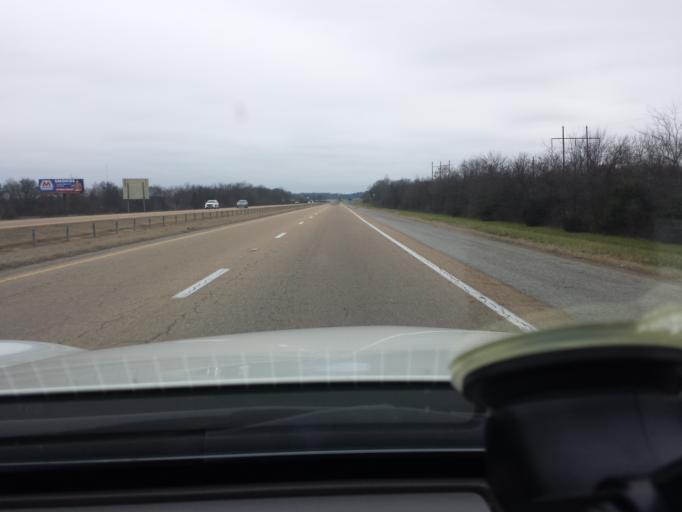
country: US
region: Mississippi
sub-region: Lee County
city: Tupelo
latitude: 34.2274
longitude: -88.7038
